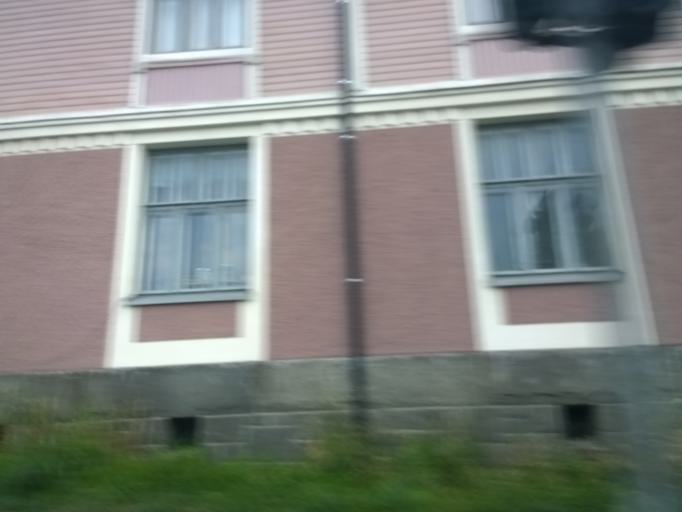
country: FI
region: Pirkanmaa
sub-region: Tampere
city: Tampere
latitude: 61.4948
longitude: 23.7727
